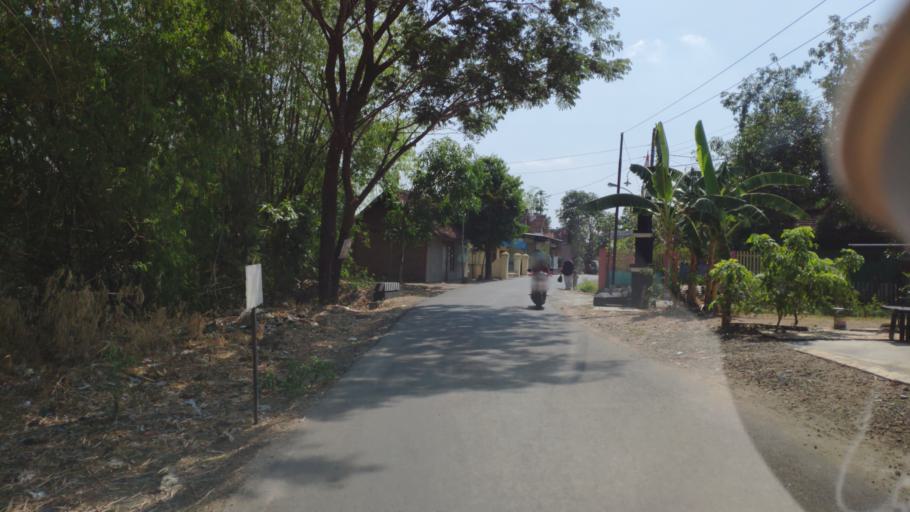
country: ID
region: Central Java
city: Beran
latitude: -6.9786
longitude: 111.4133
